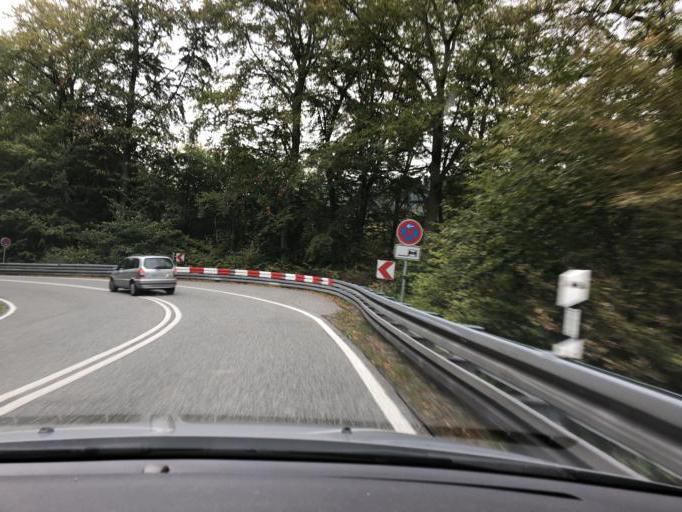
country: DE
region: Saxony-Anhalt
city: Kelbra
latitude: 51.4215
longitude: 11.0587
